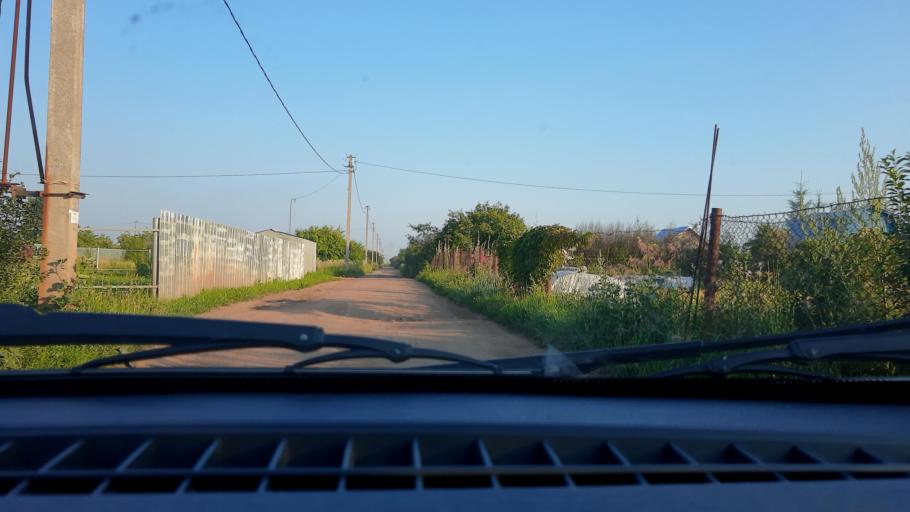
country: RU
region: Bashkortostan
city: Asanovo
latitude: 54.9482
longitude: 55.6169
